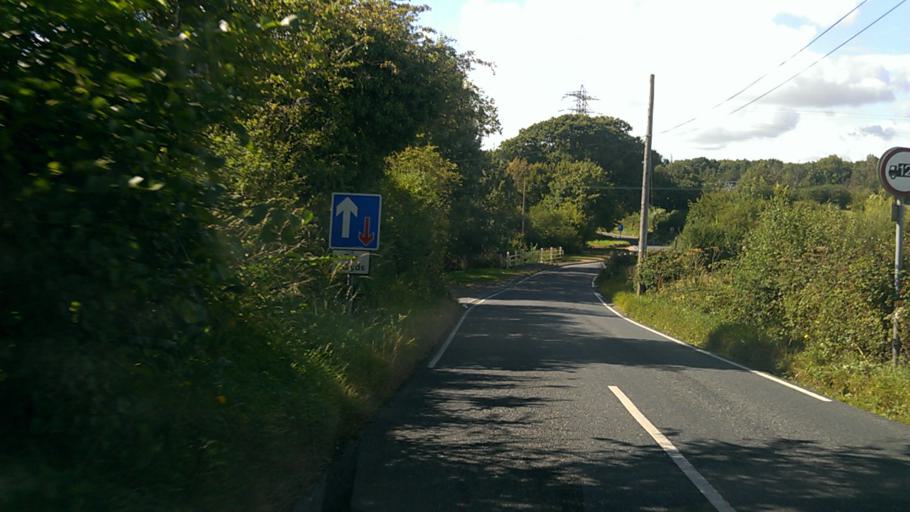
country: GB
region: England
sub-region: Essex
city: Layer de la Haye
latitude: 51.8424
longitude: 0.8900
